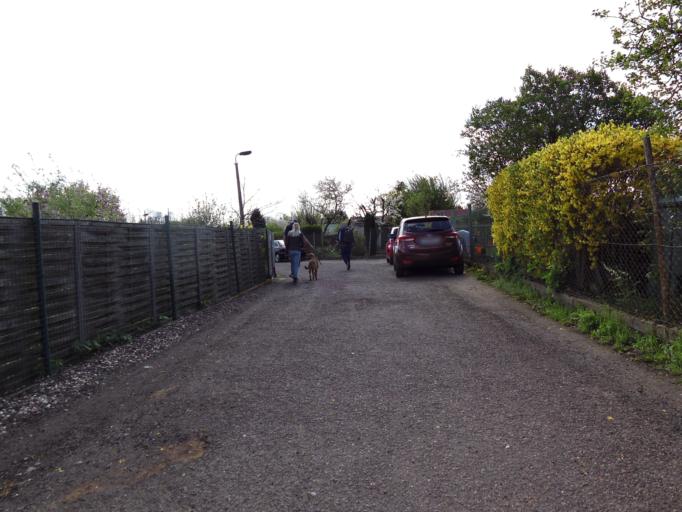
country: DE
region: Saxony
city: Leipzig
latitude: 51.3387
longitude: 12.4261
